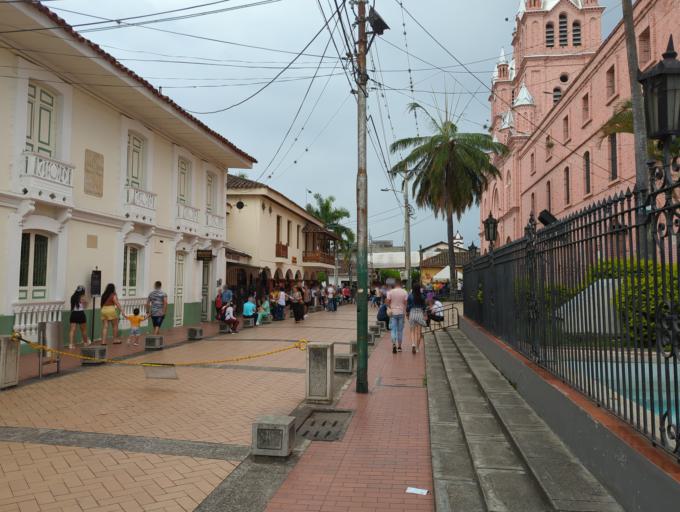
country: CO
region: Valle del Cauca
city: Buga
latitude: 3.8968
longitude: -76.3026
